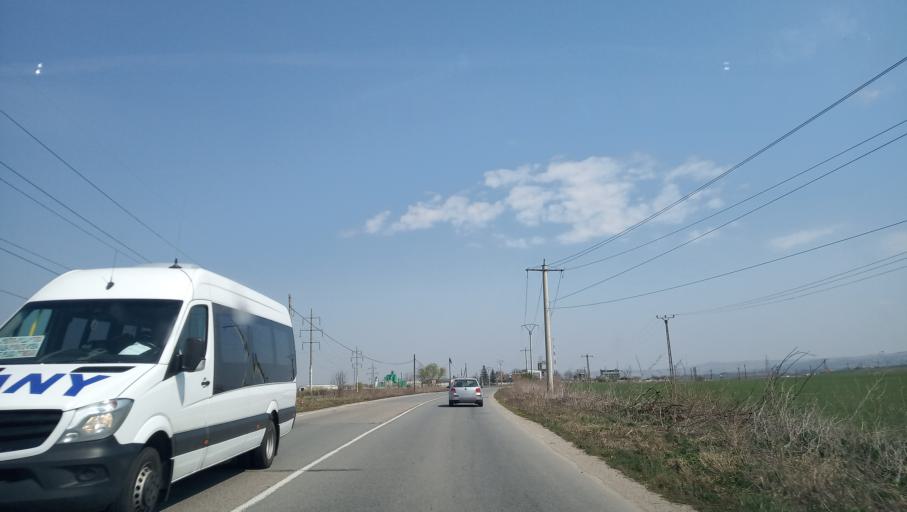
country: RO
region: Alba
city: Vurpar
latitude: 46.0151
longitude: 23.5143
